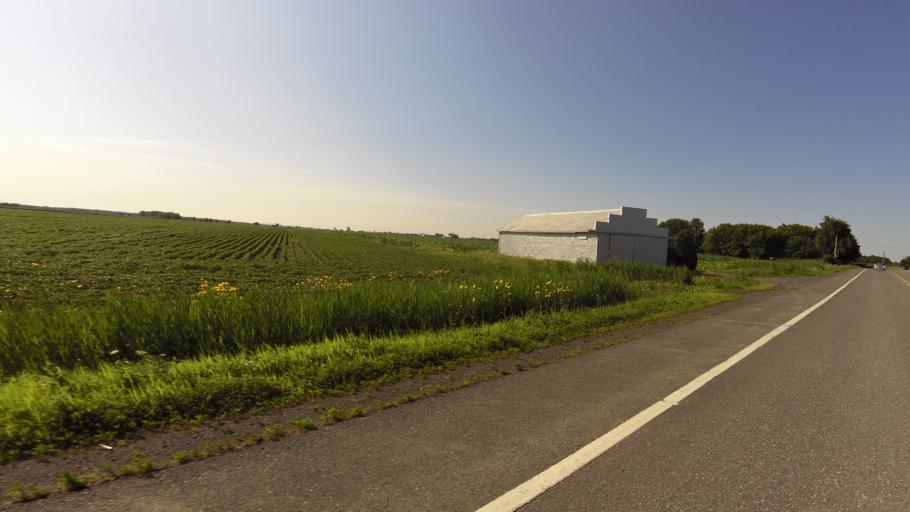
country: CA
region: Quebec
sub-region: Monteregie
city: Napierville
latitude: 45.2492
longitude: -73.3883
